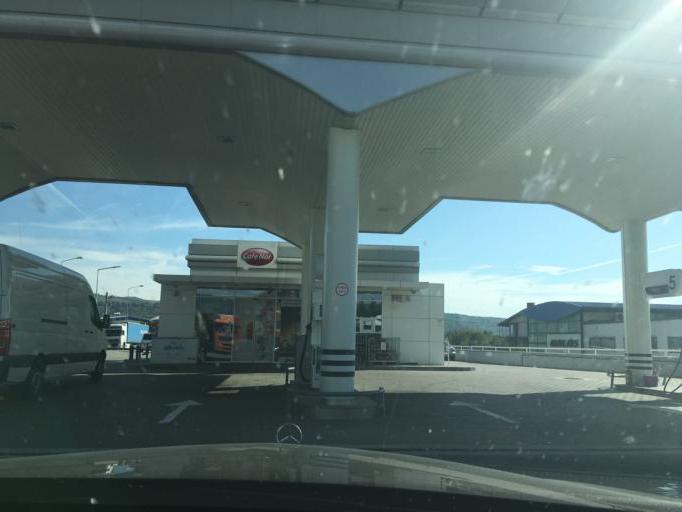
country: RO
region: Valcea
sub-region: Municipiul Ramnicu Valcea
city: Goranu
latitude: 45.1196
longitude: 24.3826
